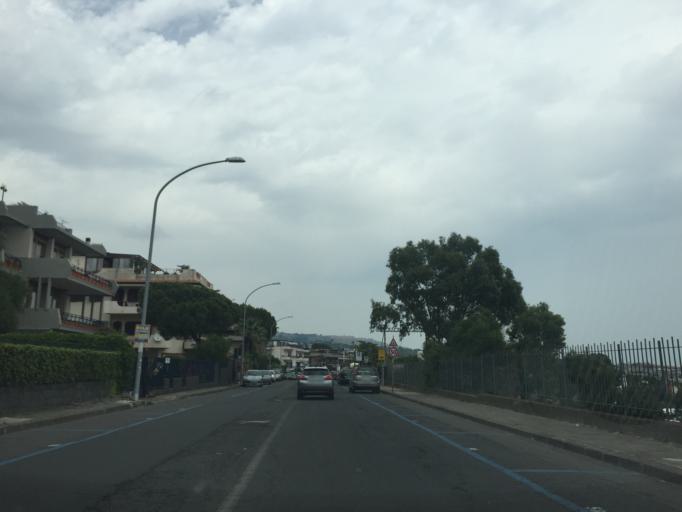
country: IT
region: Sicily
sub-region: Catania
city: Aci Castello
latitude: 37.5387
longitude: 15.1312
